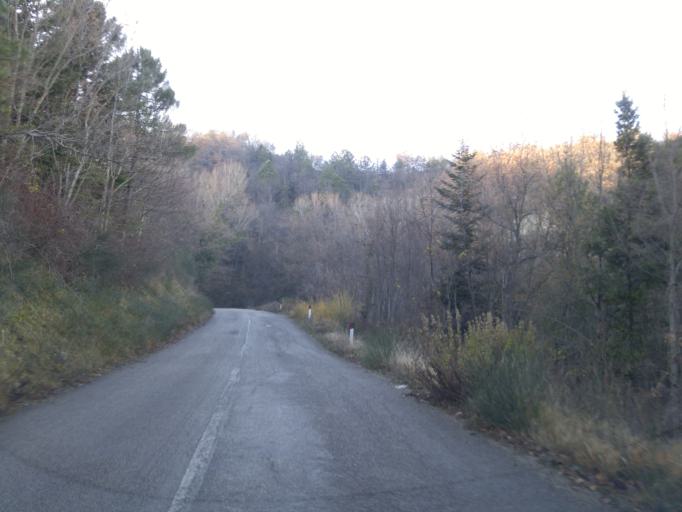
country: IT
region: The Marches
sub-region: Provincia di Pesaro e Urbino
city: Montefelcino
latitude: 43.7694
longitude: 12.8251
